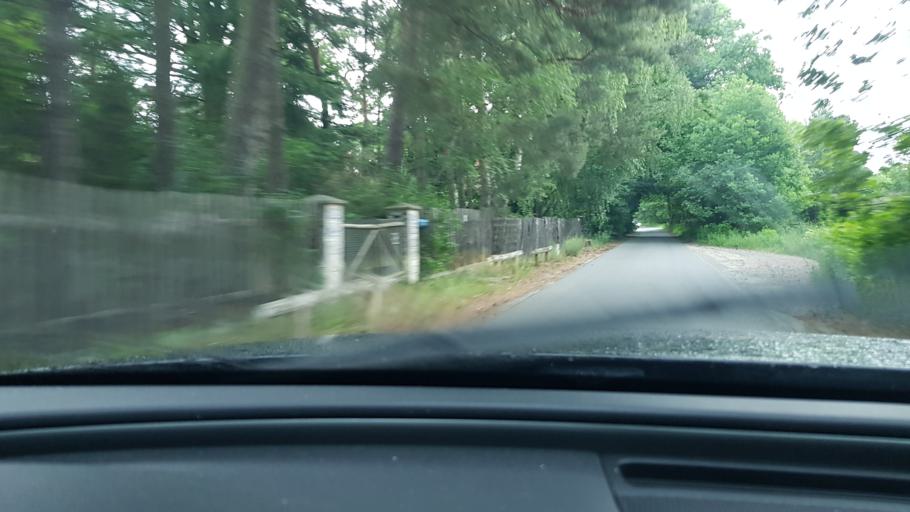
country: DE
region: Brandenburg
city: Glienicke
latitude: 52.6277
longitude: 13.3411
